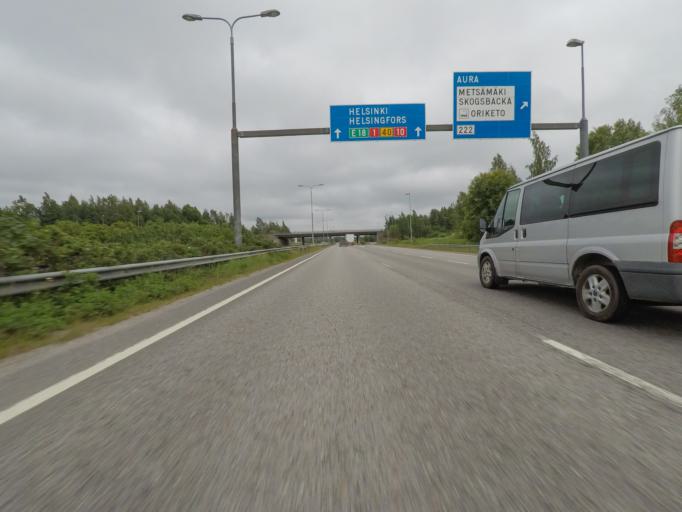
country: FI
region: Varsinais-Suomi
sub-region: Turku
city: Turku
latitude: 60.4880
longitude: 22.3183
